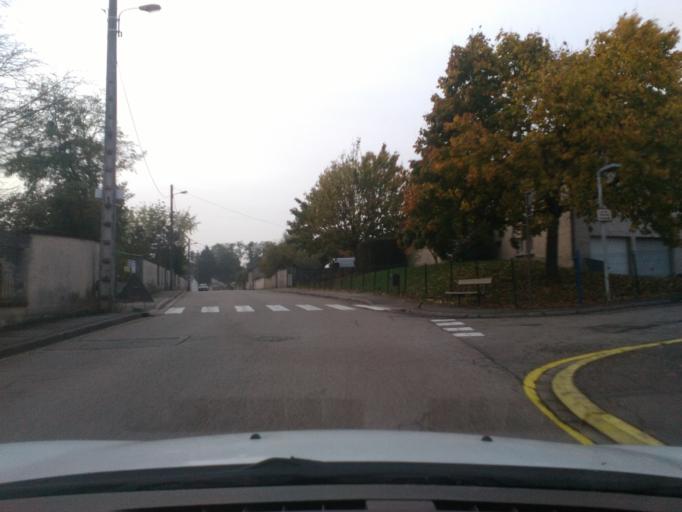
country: FR
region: Lorraine
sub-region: Departement des Vosges
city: Mirecourt
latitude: 48.3057
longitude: 6.1310
